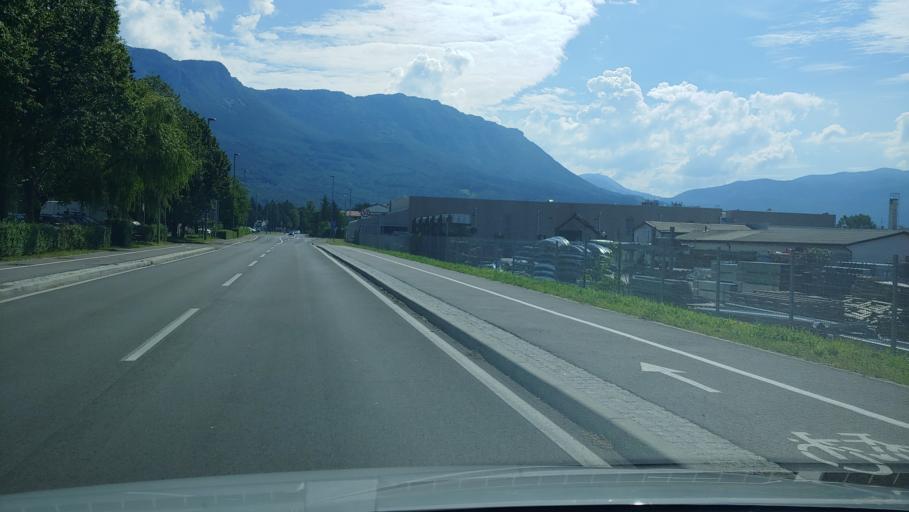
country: SI
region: Ajdovscina
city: Lokavec
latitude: 45.8866
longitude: 13.8907
